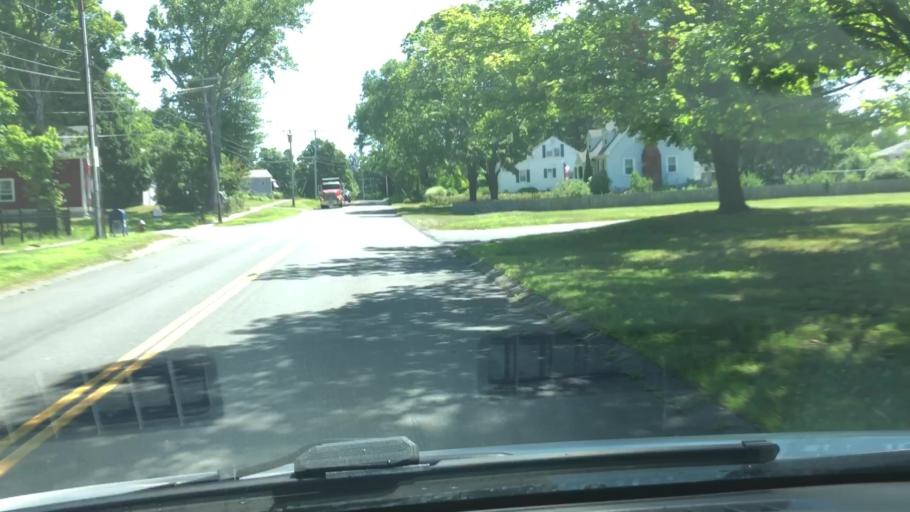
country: US
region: Massachusetts
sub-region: Hampshire County
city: Easthampton
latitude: 42.2613
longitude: -72.6777
